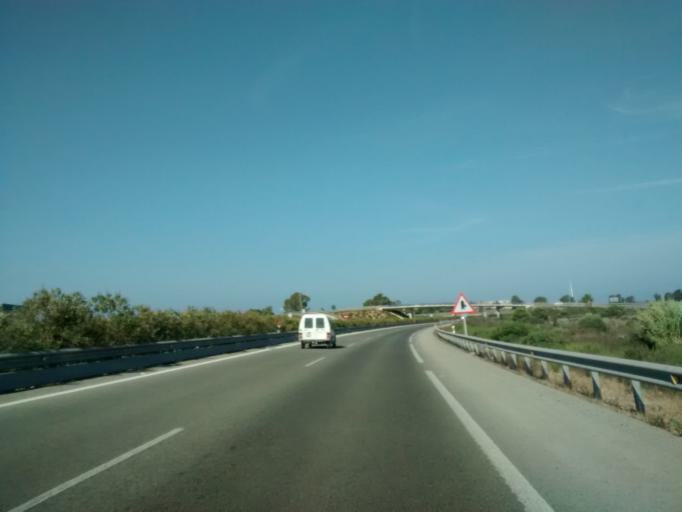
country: ES
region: Andalusia
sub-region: Provincia de Cadiz
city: Conil de la Frontera
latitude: 36.3555
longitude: -6.1003
